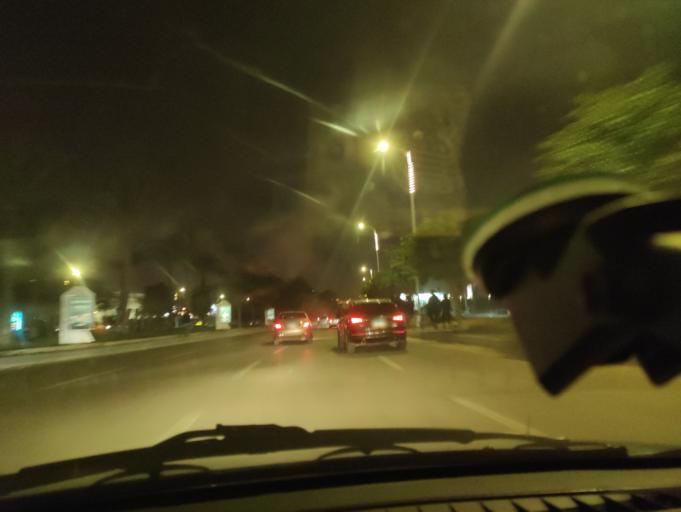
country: EG
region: Al Jizah
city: Awsim
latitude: 30.0216
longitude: 31.0053
